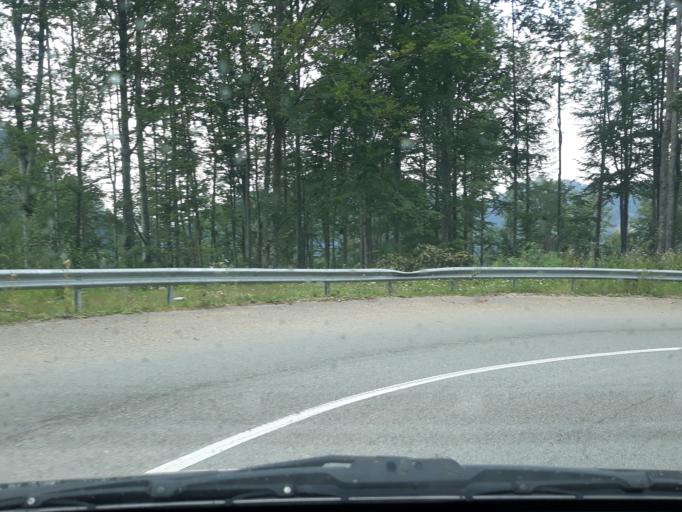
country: RO
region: Bihor
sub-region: Comuna Pietroasa
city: Pietroasa
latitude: 46.5953
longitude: 22.6588
